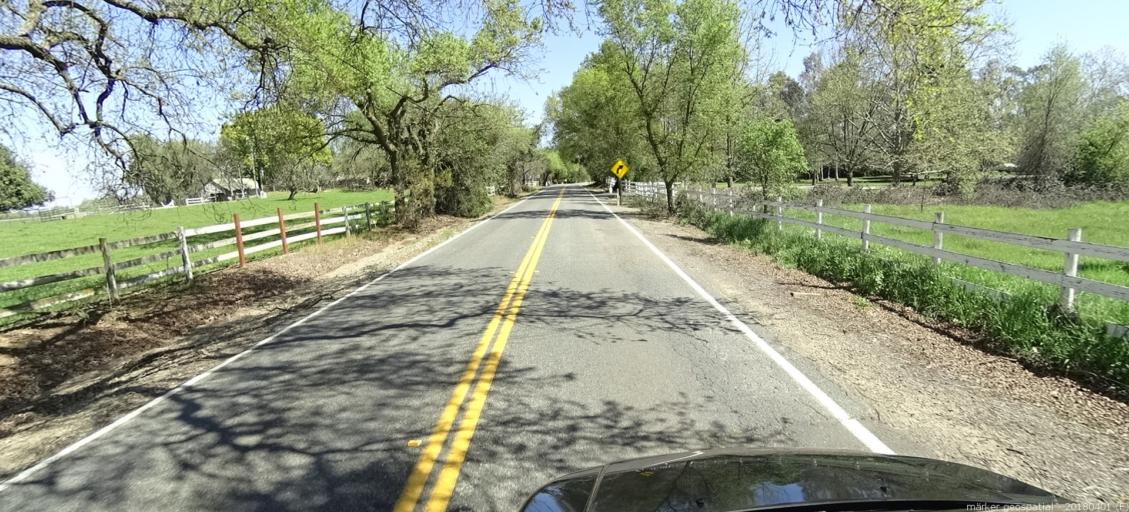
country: US
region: California
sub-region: Sacramento County
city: Wilton
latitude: 38.4157
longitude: -121.2548
